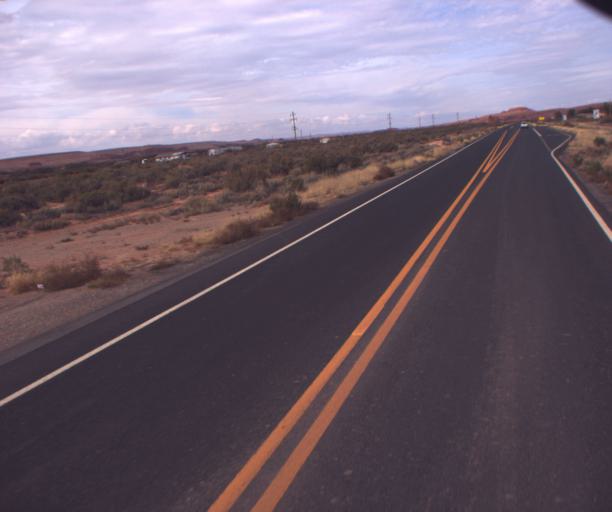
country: US
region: Arizona
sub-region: Apache County
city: Many Farms
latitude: 36.7250
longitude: -109.6296
